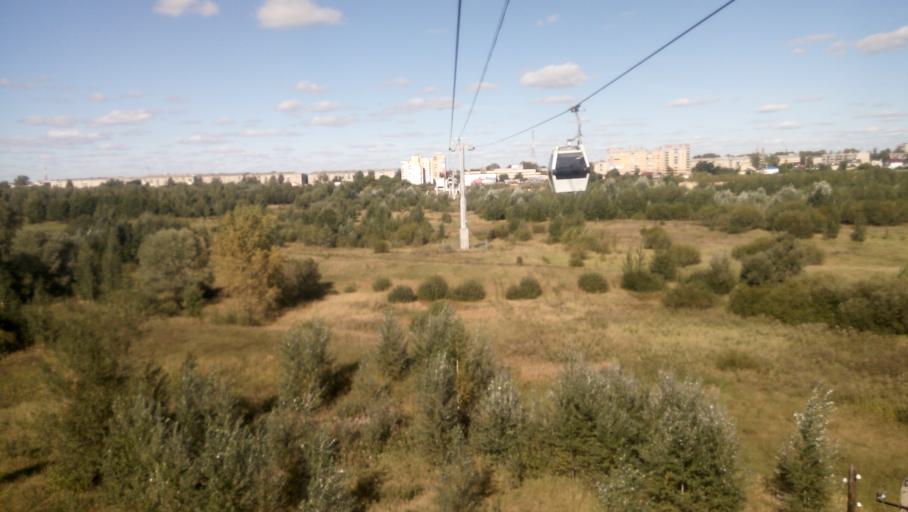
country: RU
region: Nizjnij Novgorod
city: Bor
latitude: 56.3484
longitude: 44.0570
